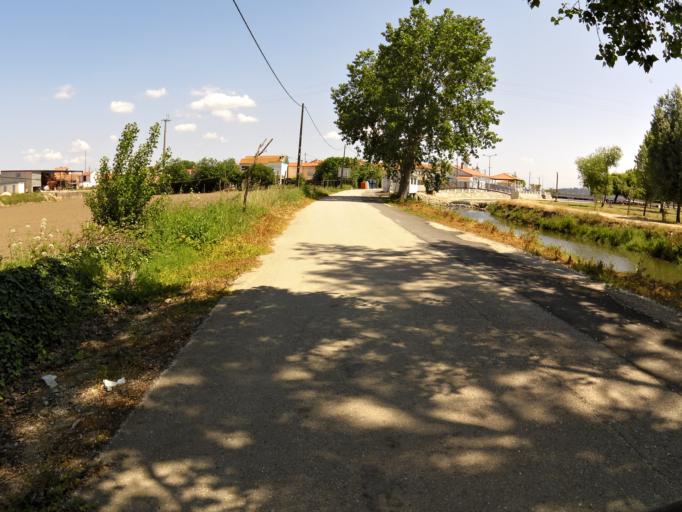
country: PT
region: Coimbra
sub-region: Montemor-O-Velho
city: Montemor-o-Velho
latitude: 40.1490
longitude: -8.7144
